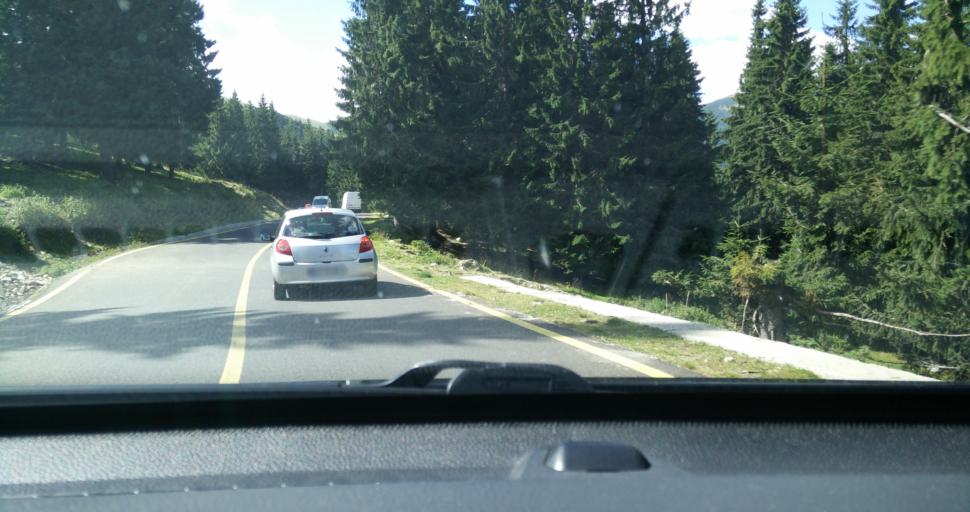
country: RO
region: Gorj
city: Novaci-Straini
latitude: 45.3910
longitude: 23.6391
